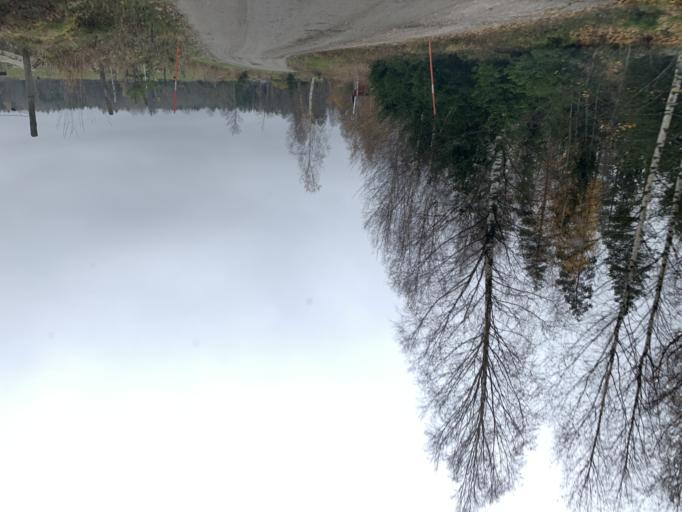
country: SE
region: Vaestmanland
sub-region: Surahammars Kommun
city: Ramnas
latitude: 59.7069
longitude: 16.0918
